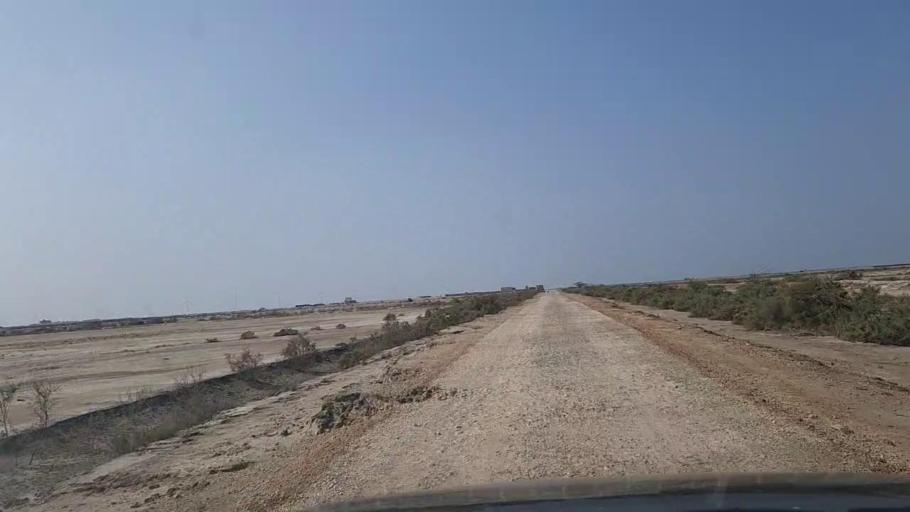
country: PK
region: Sindh
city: Gharo
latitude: 24.7074
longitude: 67.5396
